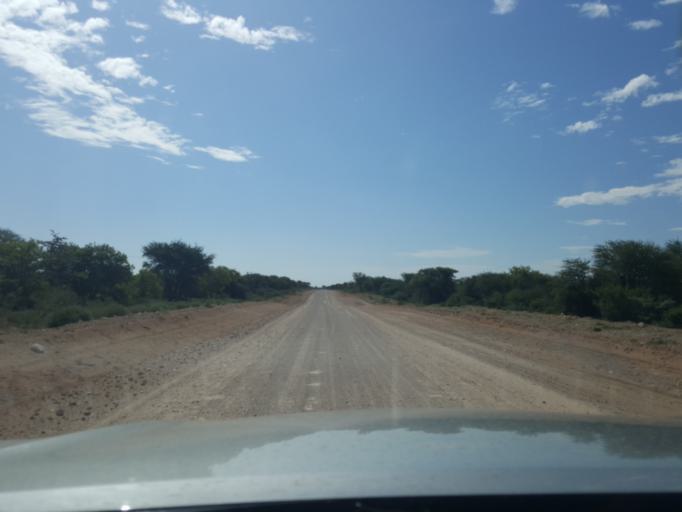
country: BW
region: Kweneng
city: Khudumelapye
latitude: -23.7881
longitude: 24.7845
